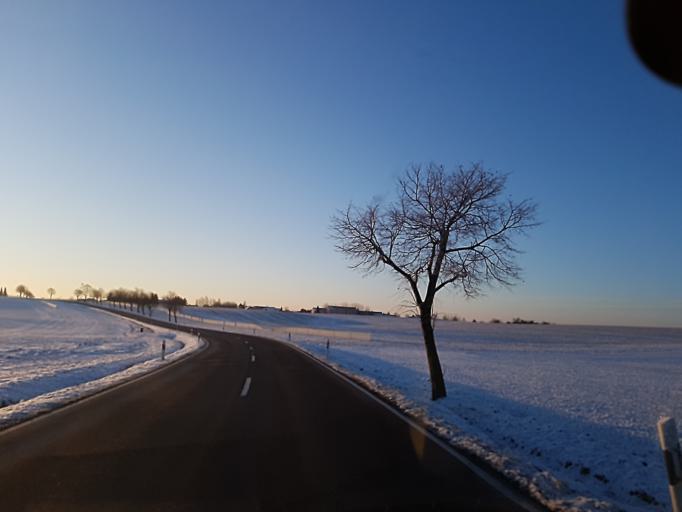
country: DE
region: Saxony
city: Grossweitzschen
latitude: 51.1658
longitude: 13.0448
